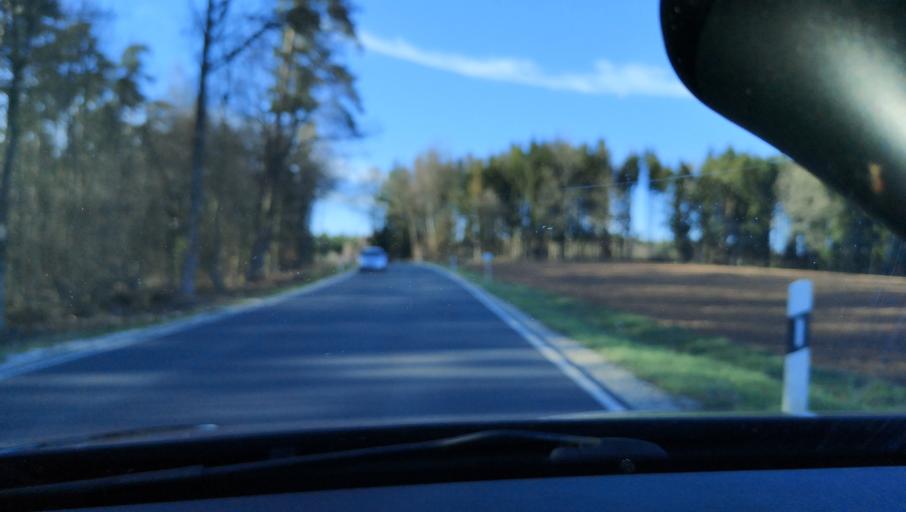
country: DE
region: Bavaria
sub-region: Upper Franconia
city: Michelau
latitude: 50.1885
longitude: 11.1171
